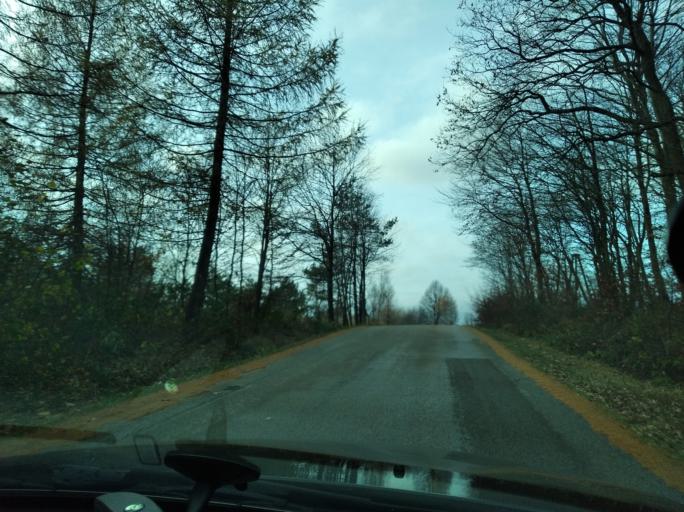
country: PL
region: Subcarpathian Voivodeship
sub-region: Powiat przeworski
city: Lopuszka Wielka
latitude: 49.8883
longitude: 22.3829
